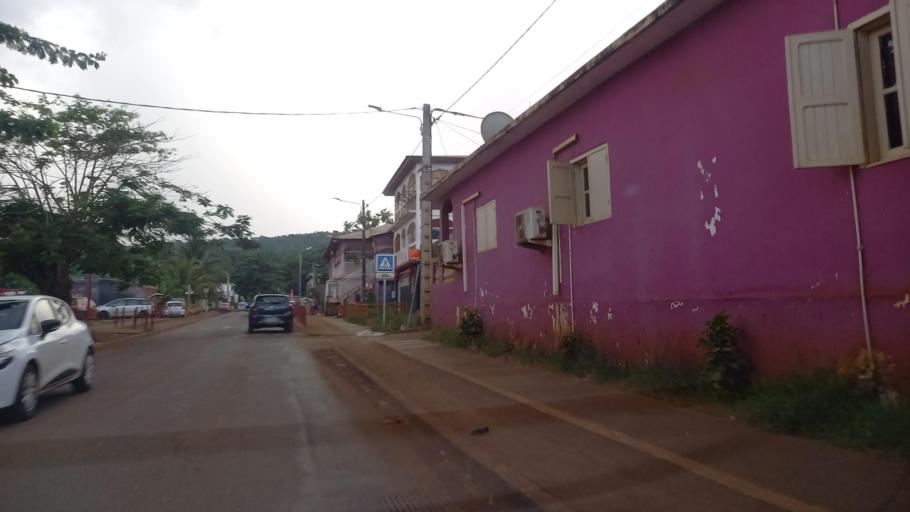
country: YT
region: Dembeni
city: Dembeni
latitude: -12.8376
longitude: 45.1746
